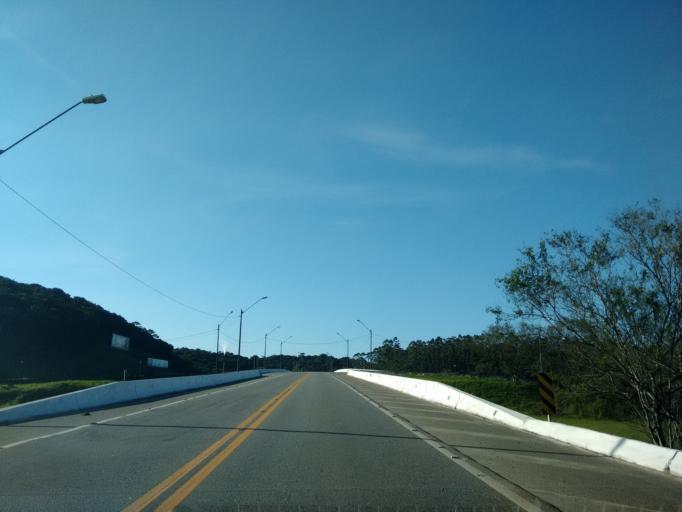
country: BR
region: Santa Catarina
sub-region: Joinville
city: Joinville
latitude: -26.4392
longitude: -48.8069
